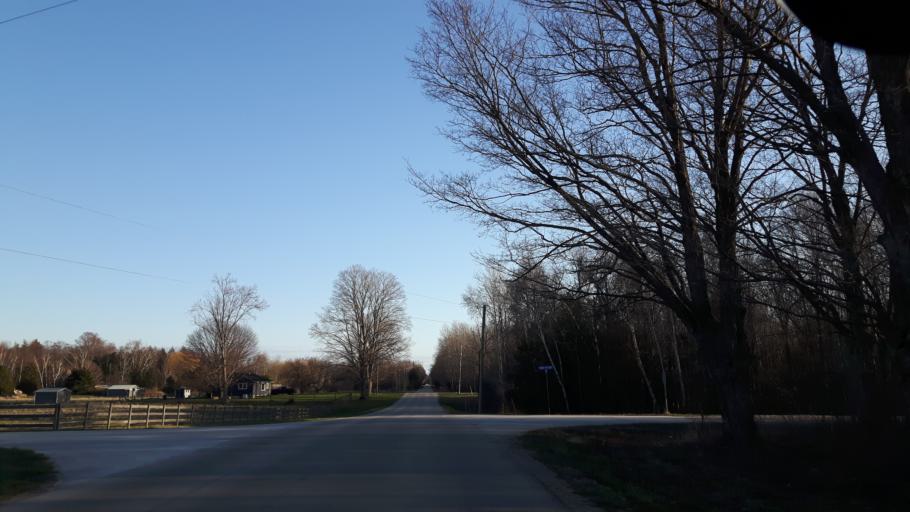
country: CA
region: Ontario
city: Goderich
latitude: 43.6245
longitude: -81.6847
